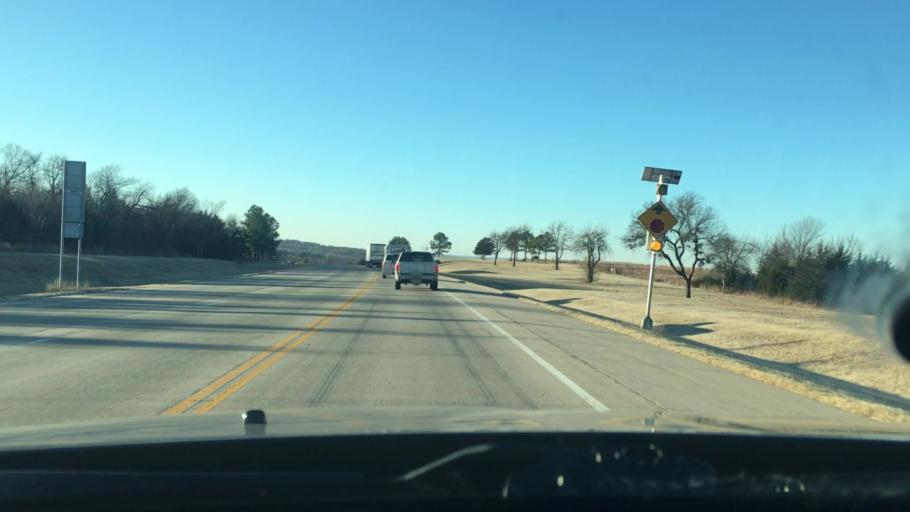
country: US
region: Oklahoma
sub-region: Murray County
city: Sulphur
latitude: 34.5125
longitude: -97.0100
